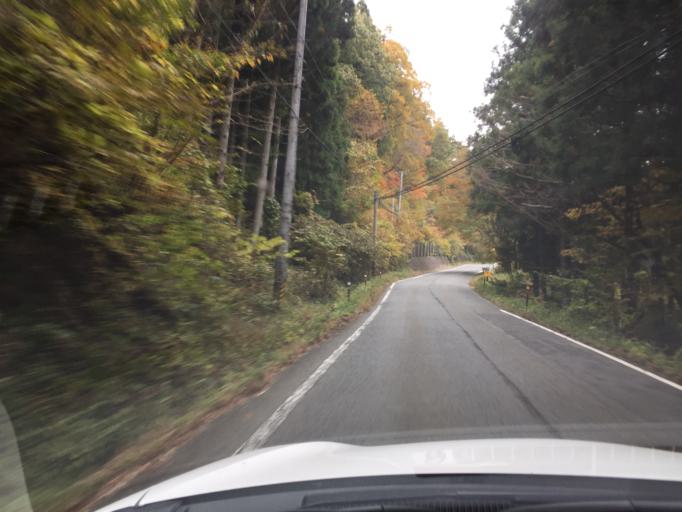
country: JP
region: Fukushima
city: Iwaki
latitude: 37.1222
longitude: 140.7761
